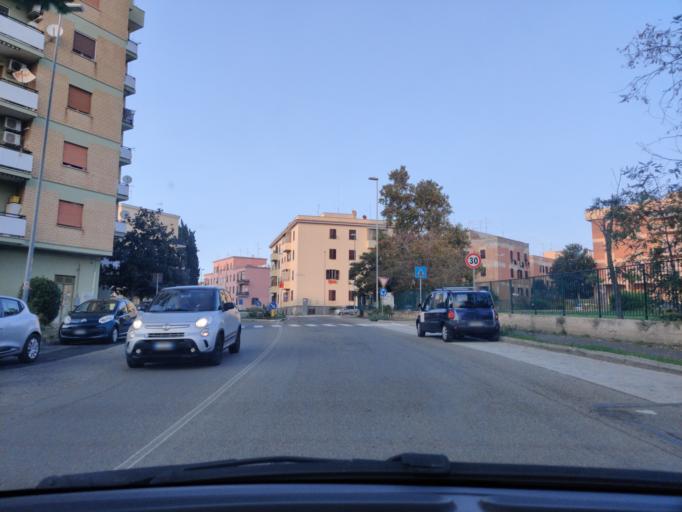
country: IT
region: Latium
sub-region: Citta metropolitana di Roma Capitale
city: Civitavecchia
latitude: 42.0877
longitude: 11.8074
